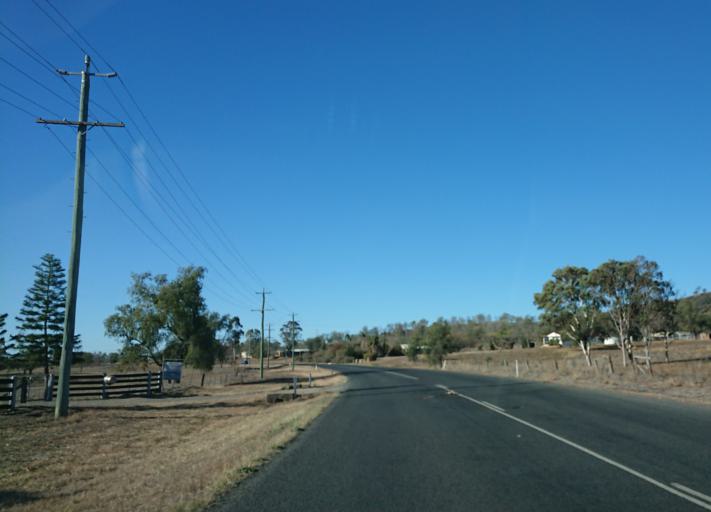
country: AU
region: Queensland
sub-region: Lockyer Valley
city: Gatton
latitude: -27.6453
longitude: 152.1813
